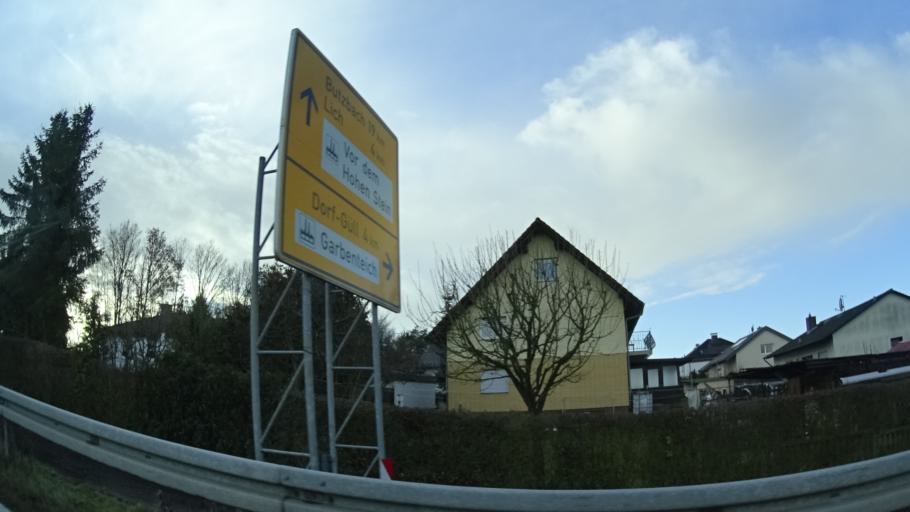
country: DE
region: Hesse
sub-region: Regierungsbezirk Giessen
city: Lich
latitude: 50.5359
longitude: 8.7606
